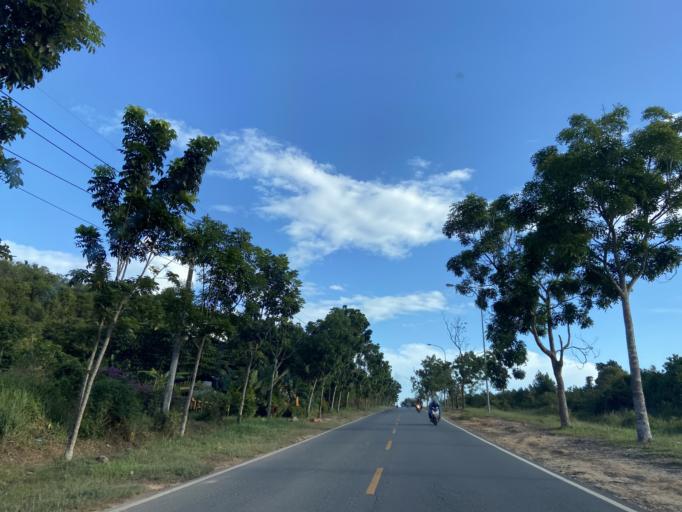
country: SG
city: Singapore
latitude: 0.9935
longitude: 104.0339
